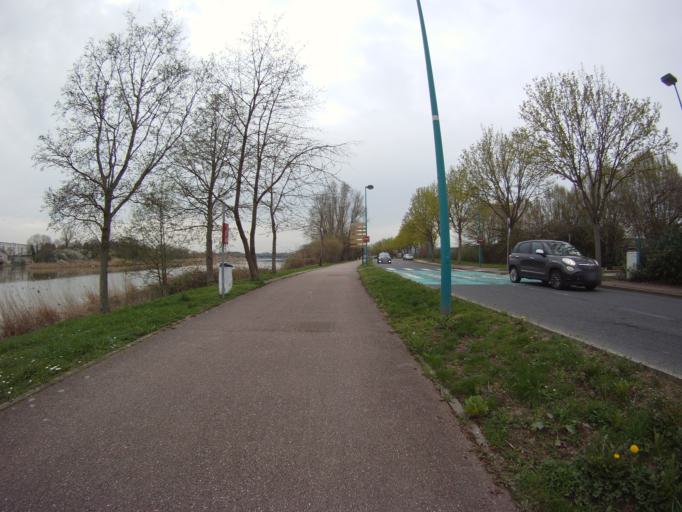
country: FR
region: Lorraine
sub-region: Departement de Meurthe-et-Moselle
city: Tomblaine
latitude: 48.6864
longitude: 6.2060
